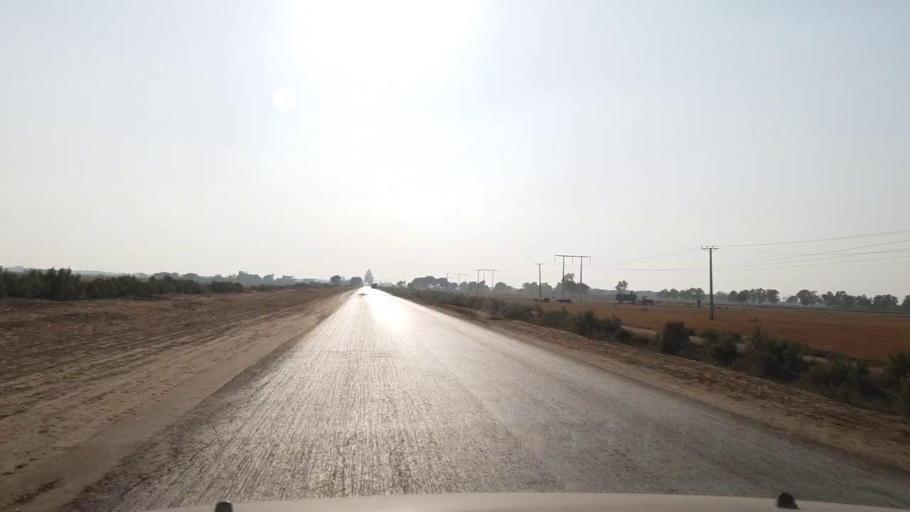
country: PK
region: Sindh
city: Bulri
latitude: 24.9877
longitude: 68.3749
